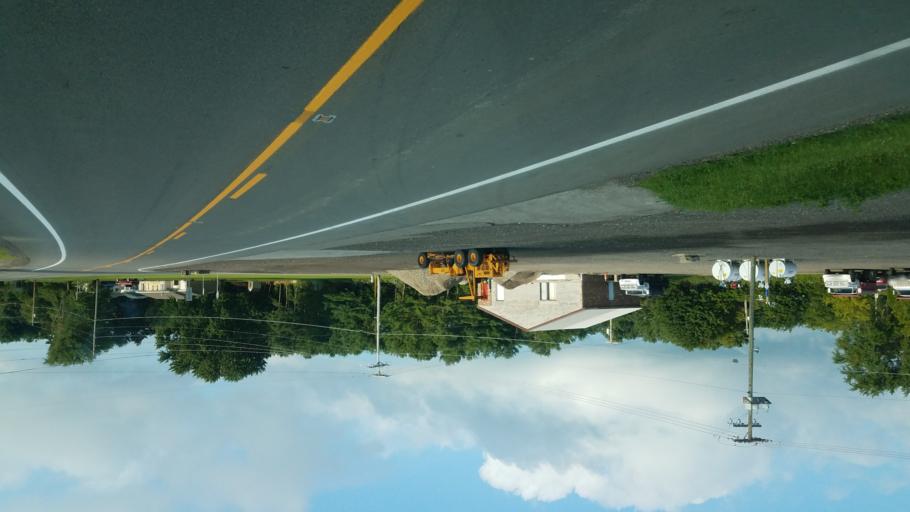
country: US
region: Ohio
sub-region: Richland County
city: Shelby
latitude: 40.8495
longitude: -82.6626
